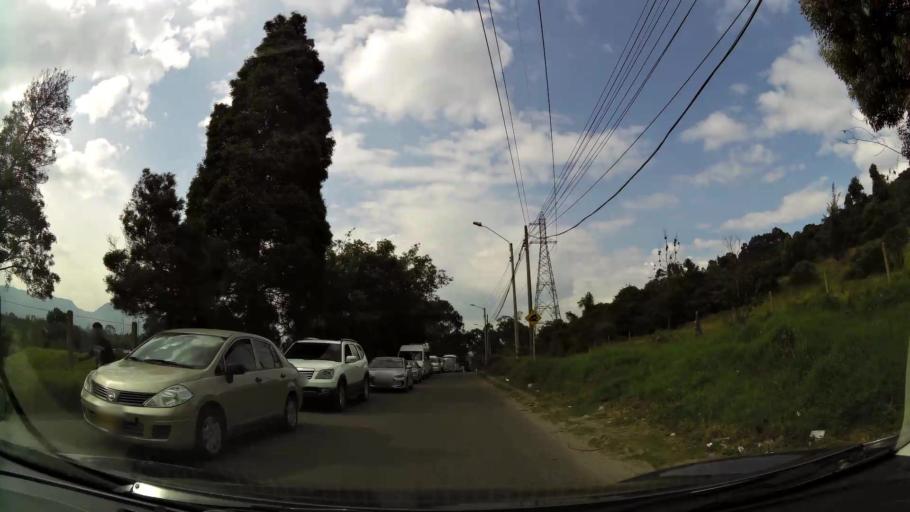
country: CO
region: Cundinamarca
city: Cota
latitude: 4.7616
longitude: -74.0770
